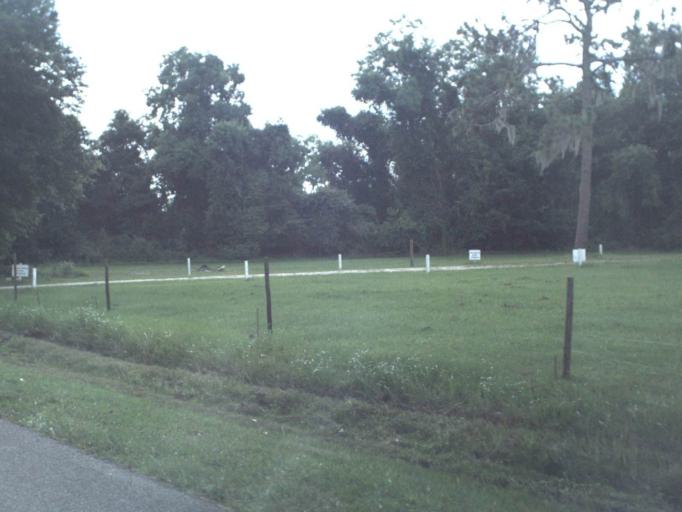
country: US
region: Florida
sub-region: Alachua County
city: Waldo
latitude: 29.6892
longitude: -82.2015
